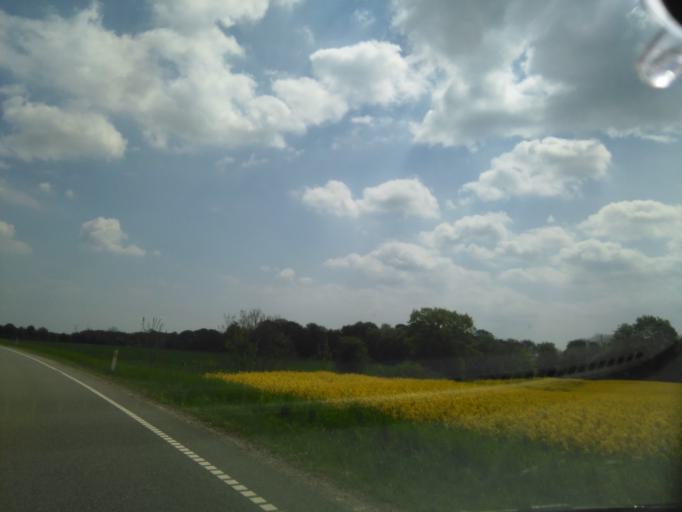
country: DK
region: Central Jutland
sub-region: Skanderborg Kommune
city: Stilling
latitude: 56.0019
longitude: 10.0021
